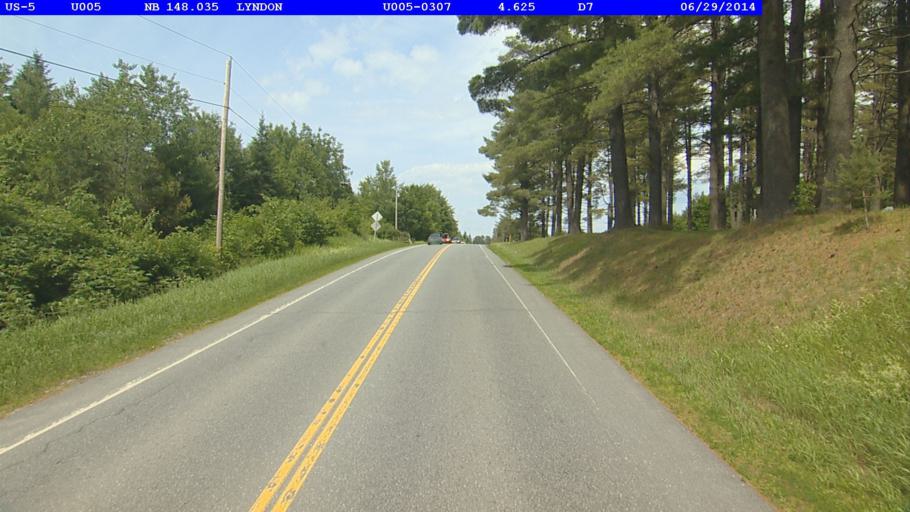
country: US
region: Vermont
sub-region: Caledonia County
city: Lyndonville
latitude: 44.5559
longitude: -71.9975
